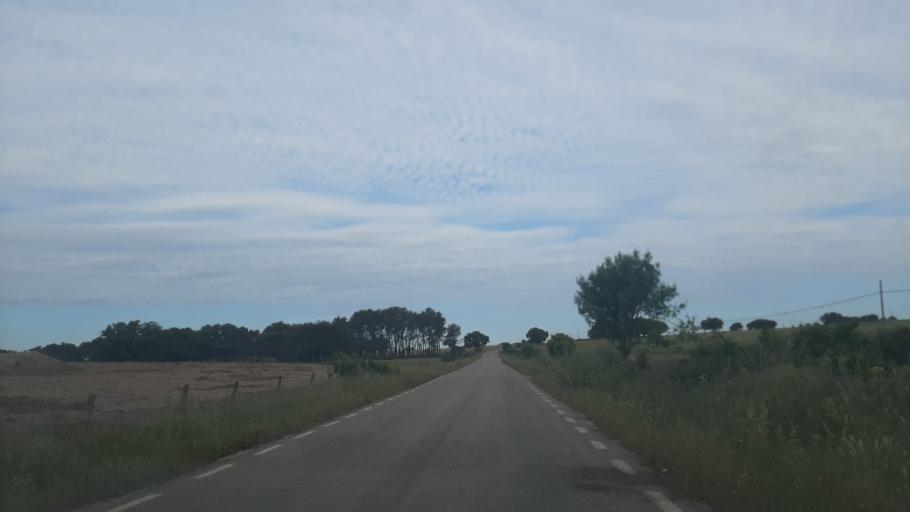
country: ES
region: Castille and Leon
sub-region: Provincia de Salamanca
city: Gallegos de Arganan
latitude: 40.6425
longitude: -6.7372
